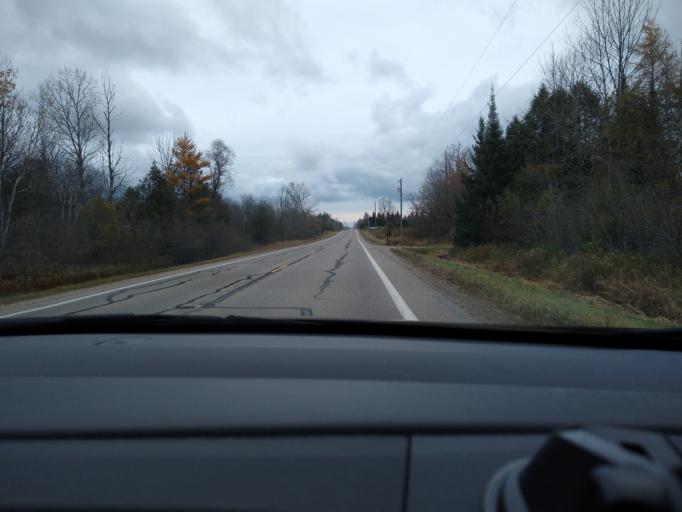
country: US
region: Michigan
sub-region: Delta County
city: Escanaba
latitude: 45.7663
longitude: -87.3057
